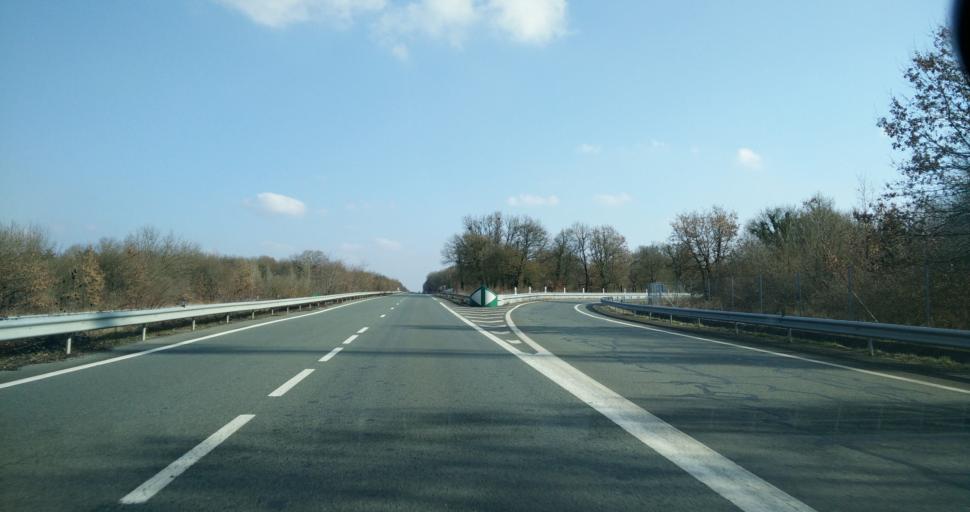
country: FR
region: Poitou-Charentes
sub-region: Departement de la Charente-Maritime
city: Courcon
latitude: 46.2216
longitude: -0.8126
